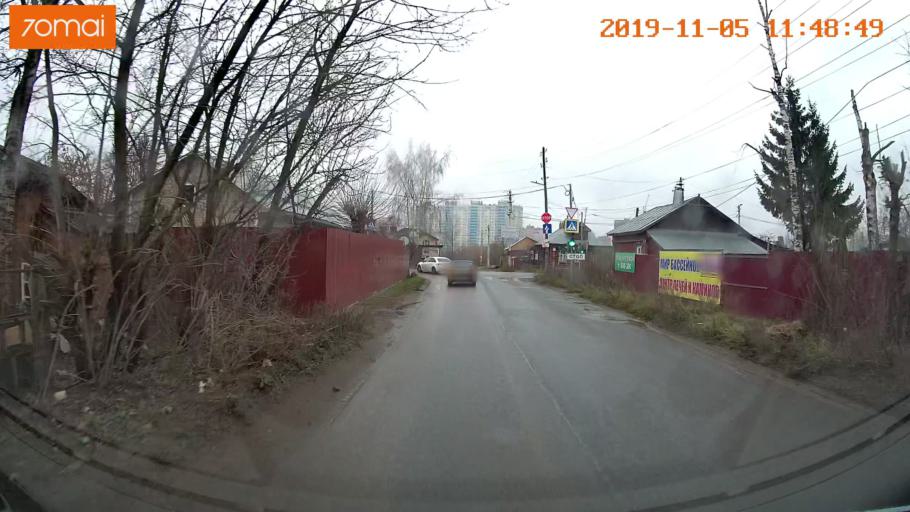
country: RU
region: Ivanovo
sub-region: Gorod Ivanovo
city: Ivanovo
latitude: 57.0069
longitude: 40.9980
